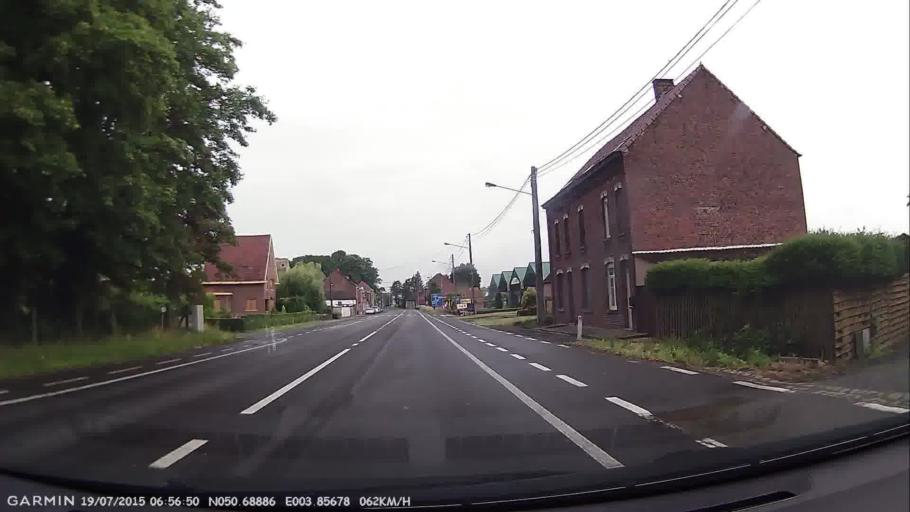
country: BE
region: Wallonia
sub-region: Province du Hainaut
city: Lessines
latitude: 50.6888
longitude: 3.8568
